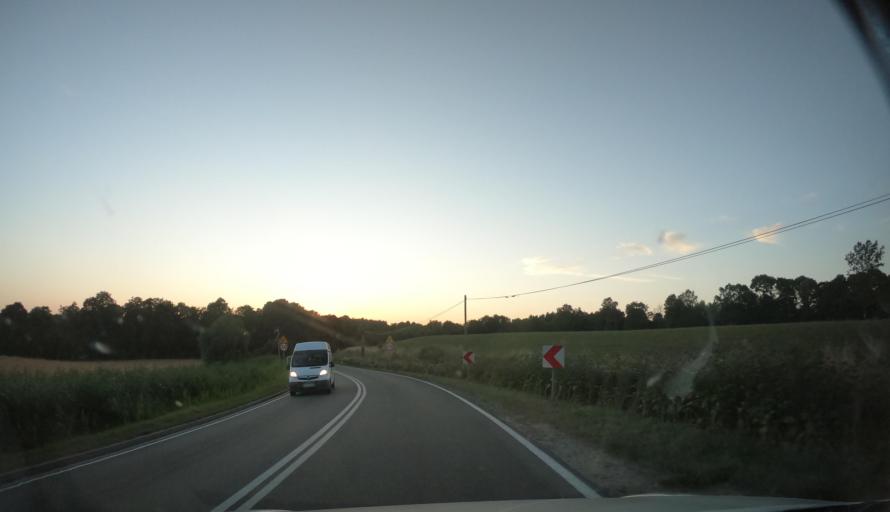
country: PL
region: Kujawsko-Pomorskie
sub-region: Powiat bydgoski
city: Koronowo
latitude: 53.3563
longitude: 17.8647
